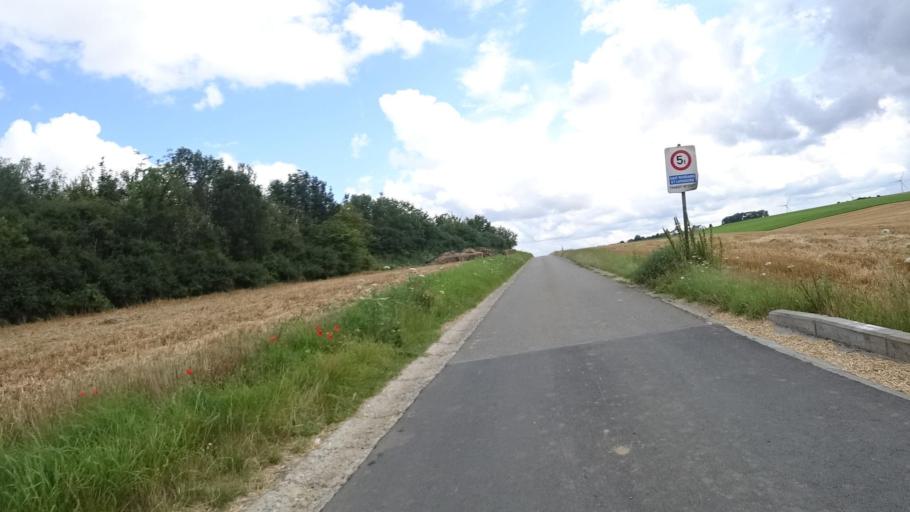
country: BE
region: Wallonia
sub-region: Province du Brabant Wallon
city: Villers-la-Ville
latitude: 50.5580
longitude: 4.5258
